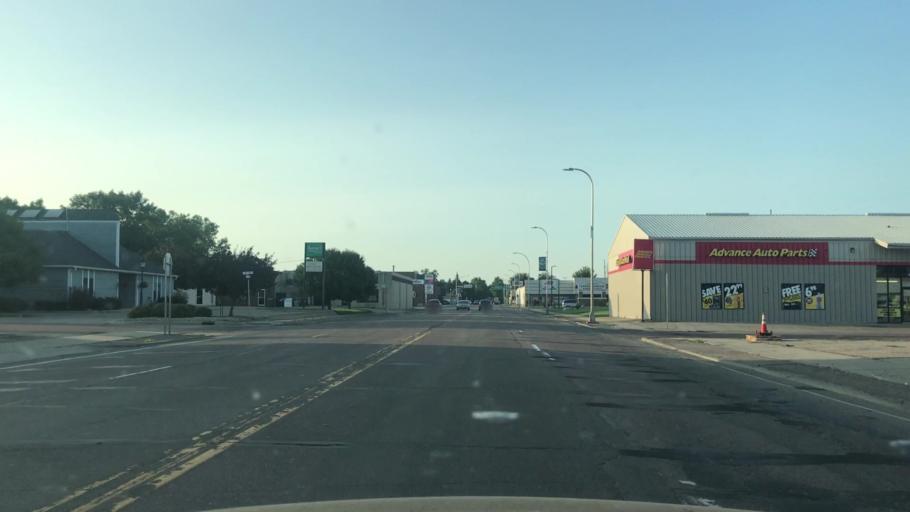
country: US
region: Minnesota
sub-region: Cottonwood County
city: Windom
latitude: 43.8639
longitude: -95.1149
